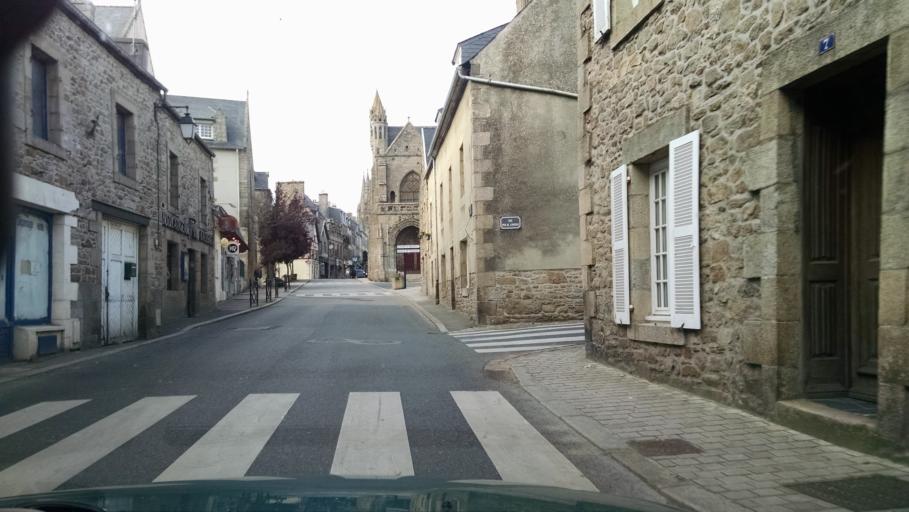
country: FR
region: Brittany
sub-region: Departement du Finistere
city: Saint-Pol-de-Leon
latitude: 48.6820
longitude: -3.9871
